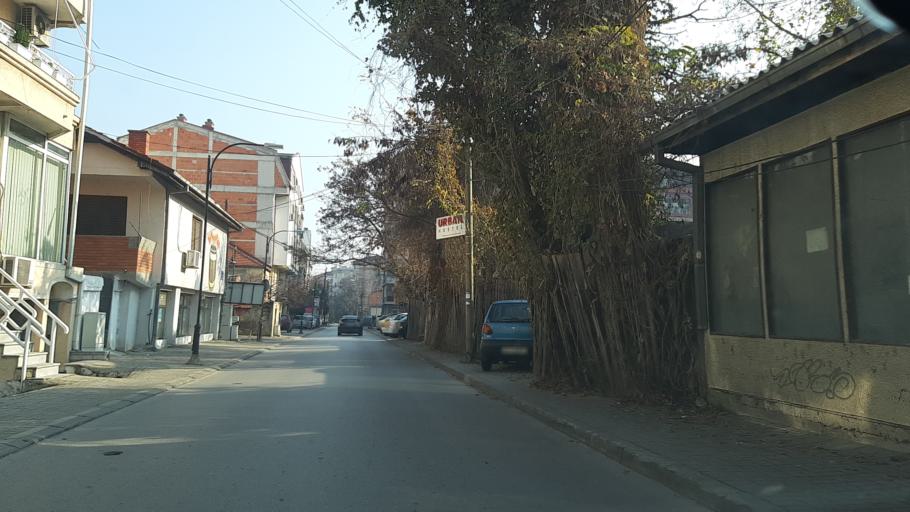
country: MK
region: Karpos
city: Skopje
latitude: 41.9987
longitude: 21.4137
